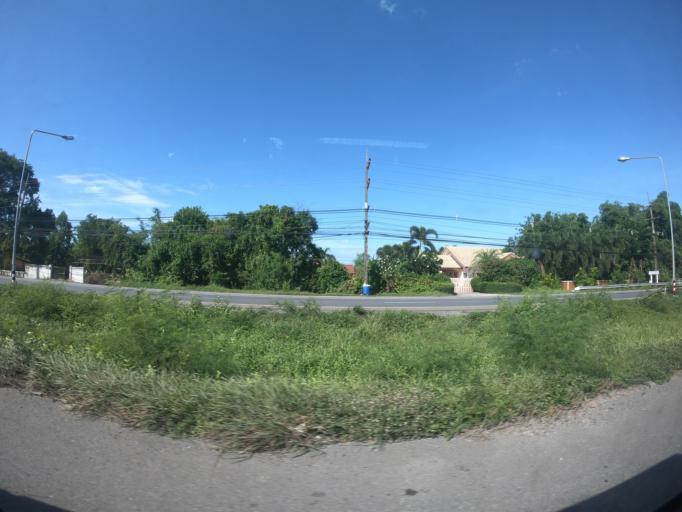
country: TH
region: Nakhon Nayok
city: Ban Na
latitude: 14.2440
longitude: 101.1123
